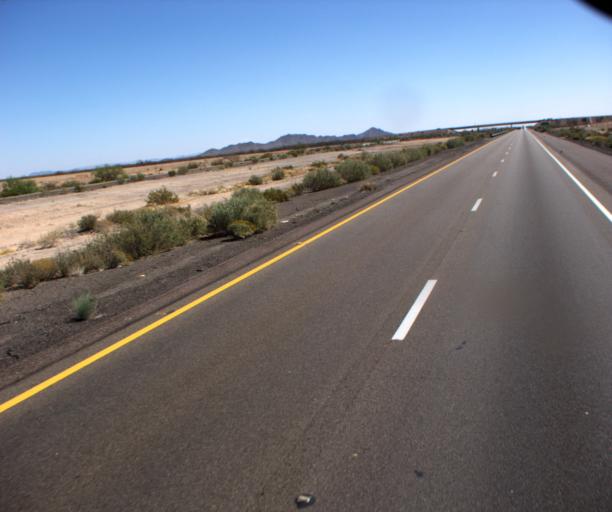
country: US
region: Arizona
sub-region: La Paz County
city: Salome
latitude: 33.5960
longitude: -113.5343
